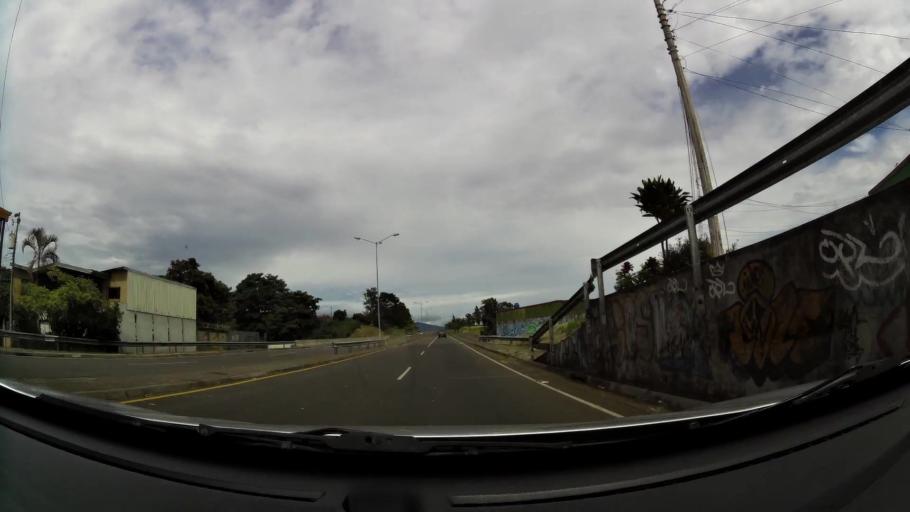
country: CR
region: San Jose
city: Alajuelita
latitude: 9.9059
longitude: -84.0757
